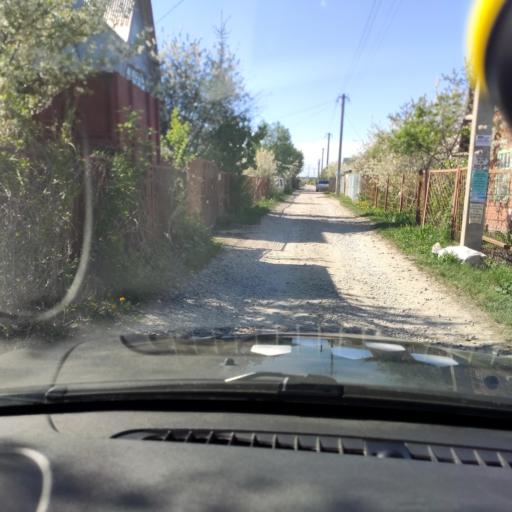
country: RU
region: Samara
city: Tol'yatti
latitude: 53.5940
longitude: 49.2894
